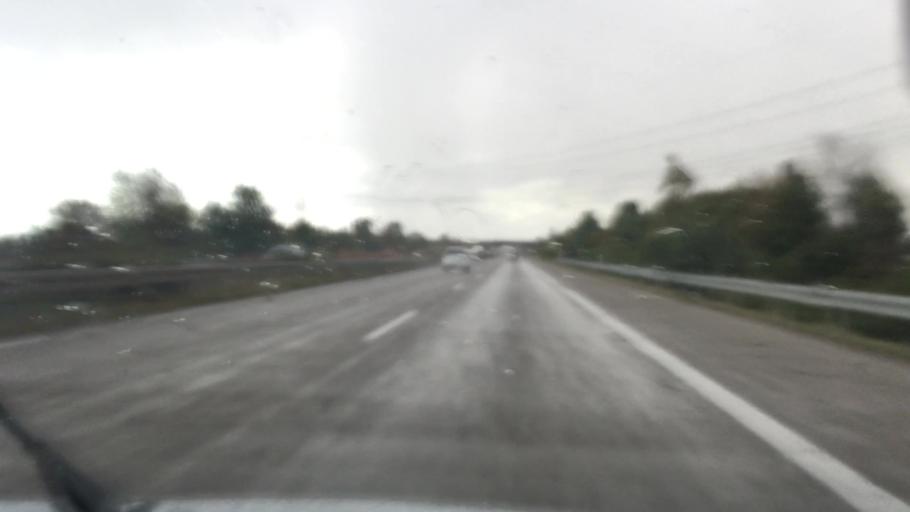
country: DE
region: Saxony-Anhalt
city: Biere
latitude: 51.9830
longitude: 11.6680
